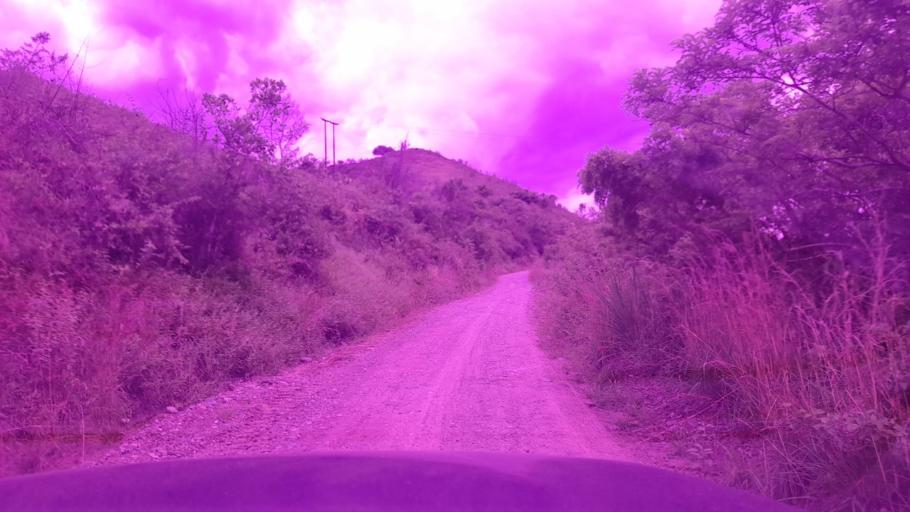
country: CO
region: Valle del Cauca
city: Andalucia
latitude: 4.1749
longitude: -76.1246
